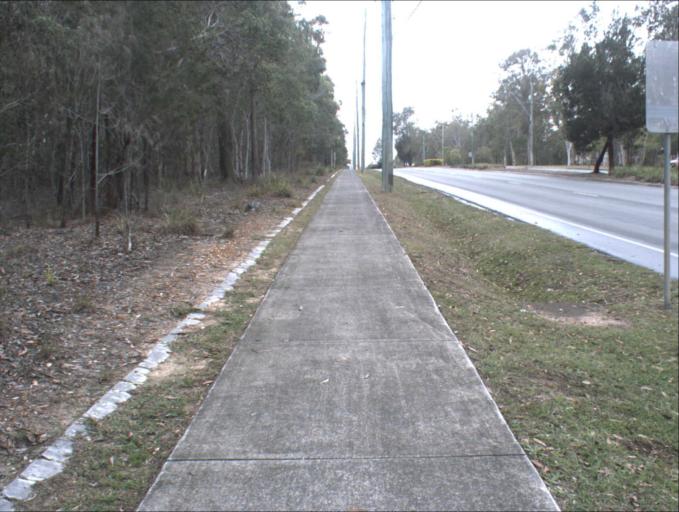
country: AU
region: Queensland
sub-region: Logan
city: Woodridge
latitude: -27.6727
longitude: 153.0753
